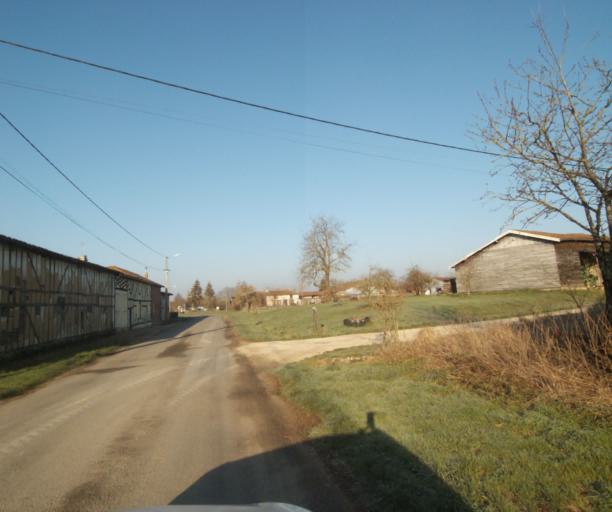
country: FR
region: Champagne-Ardenne
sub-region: Departement de la Haute-Marne
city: Montier-en-Der
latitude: 48.5025
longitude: 4.7295
